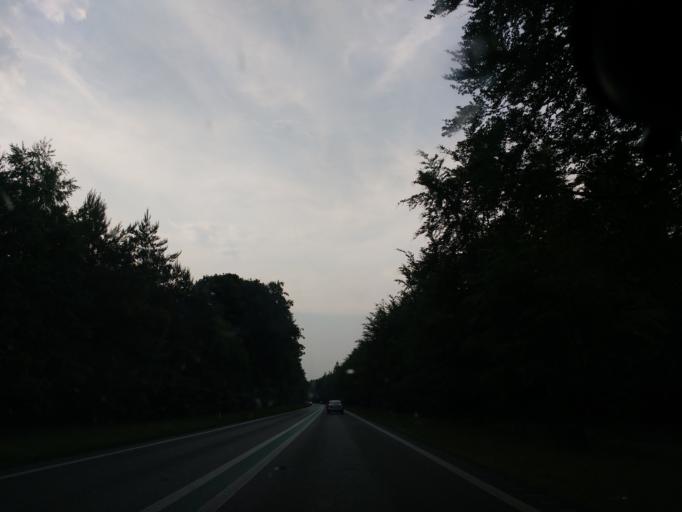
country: NL
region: Drenthe
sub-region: Gemeente Borger-Odoorn
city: Borger
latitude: 52.8678
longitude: 6.8350
